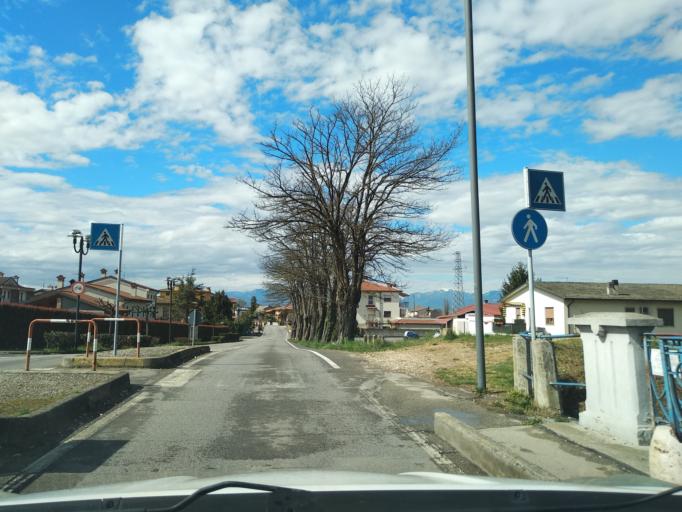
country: IT
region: Veneto
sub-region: Provincia di Vicenza
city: Bolzano Vicentino
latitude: 45.6010
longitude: 11.6206
